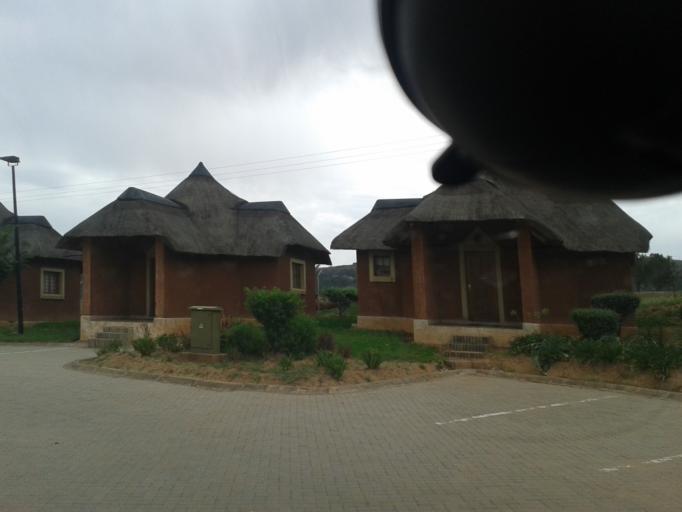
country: LS
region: Maseru
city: Maseru
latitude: -29.3434
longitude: 27.6626
